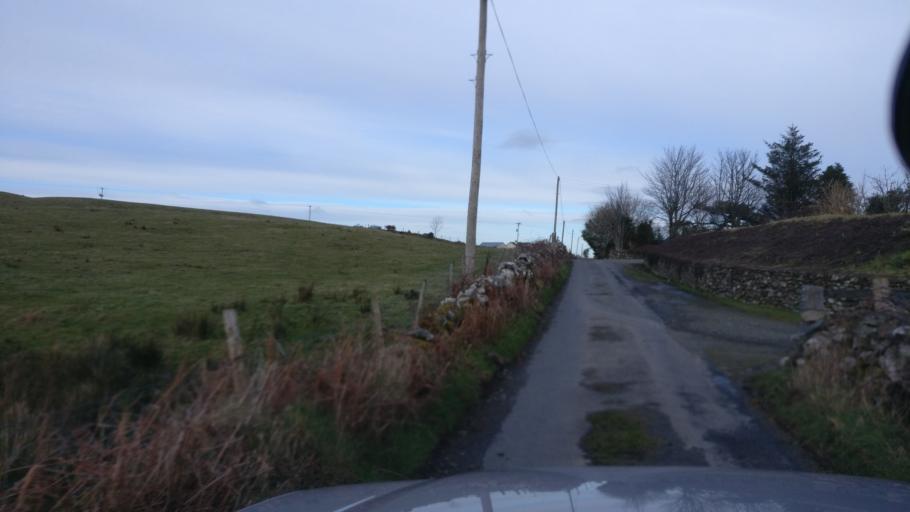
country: IE
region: Connaught
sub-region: County Galway
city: Oughterard
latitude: 53.5283
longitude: -9.3715
